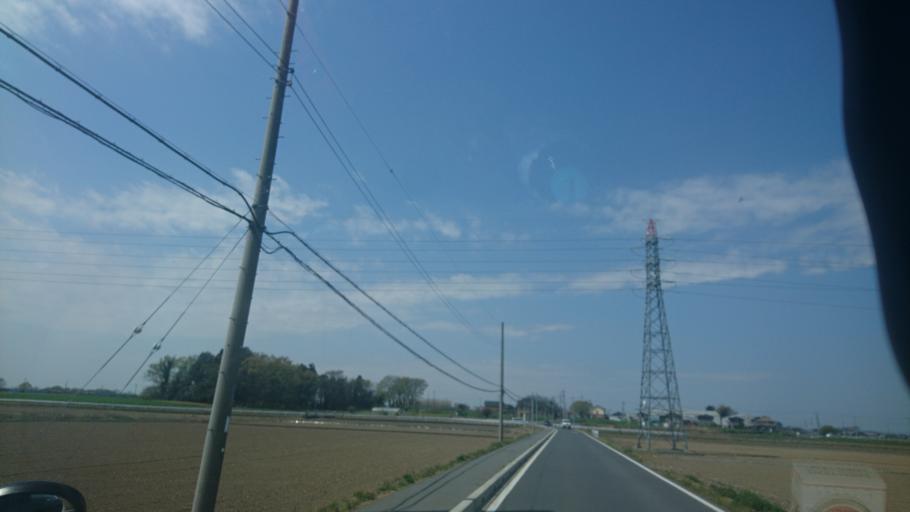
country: JP
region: Ibaraki
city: Yuki
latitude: 36.2203
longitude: 139.9280
